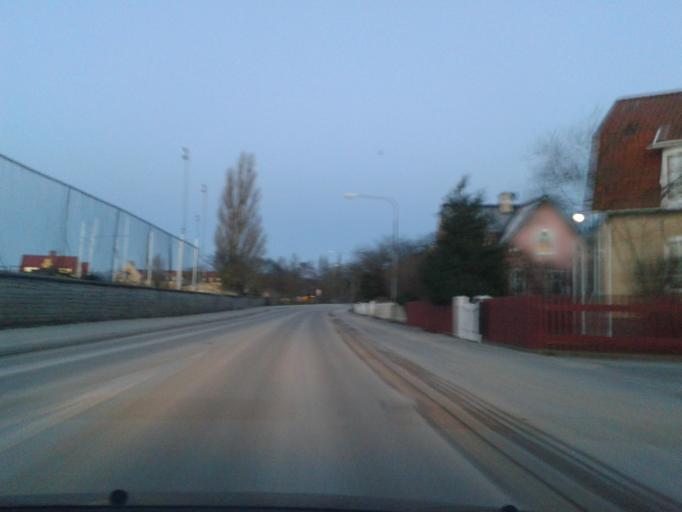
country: SE
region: Gotland
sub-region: Gotland
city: Visby
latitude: 57.6339
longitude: 18.2966
